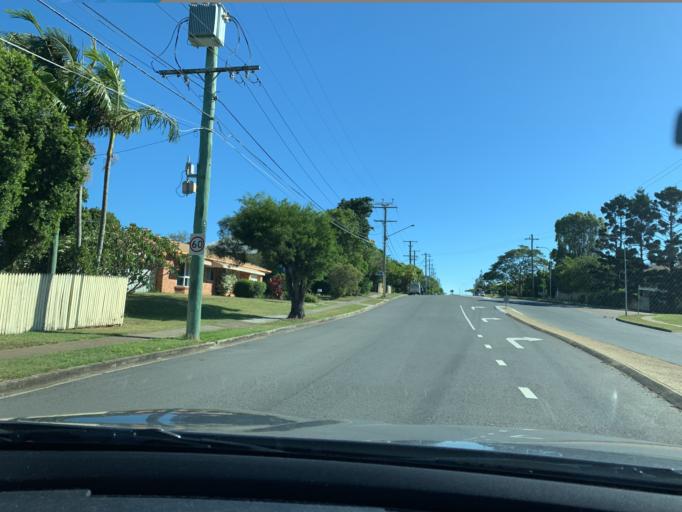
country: AU
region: Queensland
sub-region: Brisbane
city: Wynnum
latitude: -27.4275
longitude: 153.1635
